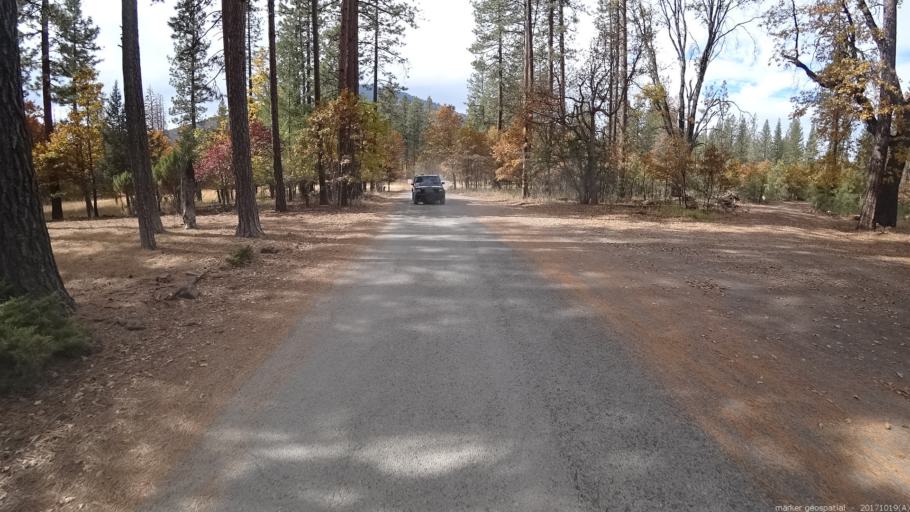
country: US
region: California
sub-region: Shasta County
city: Burney
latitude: 41.0799
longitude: -121.5299
